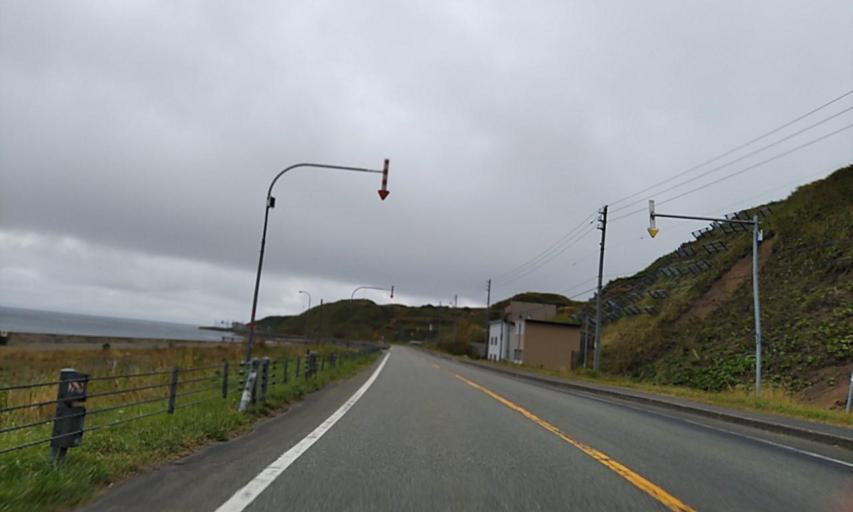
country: JP
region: Hokkaido
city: Makubetsu
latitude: 45.5168
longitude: 141.9262
